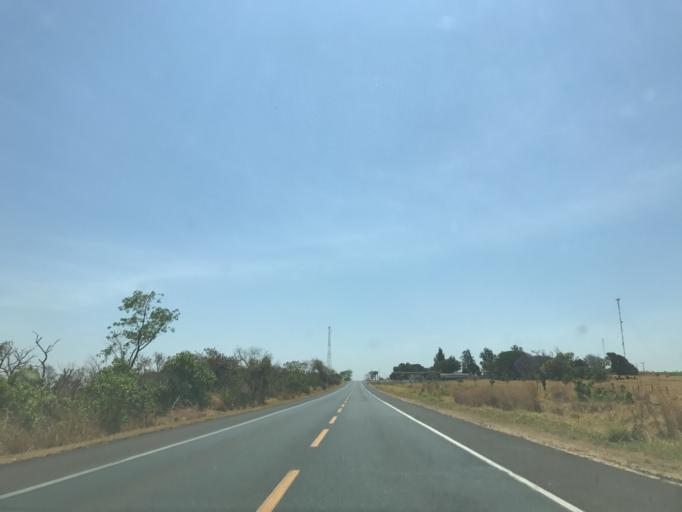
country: BR
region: Minas Gerais
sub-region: Frutal
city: Frutal
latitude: -19.8447
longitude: -48.9637
